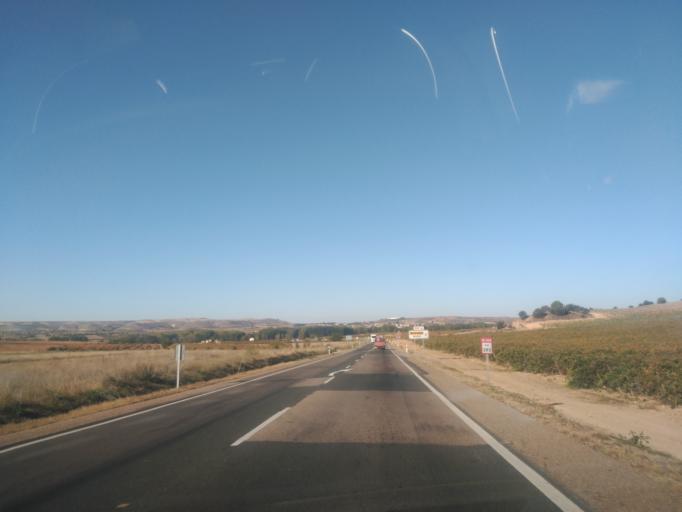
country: ES
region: Castille and Leon
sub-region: Provincia de Burgos
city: Haza
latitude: 41.6361
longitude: -3.8261
